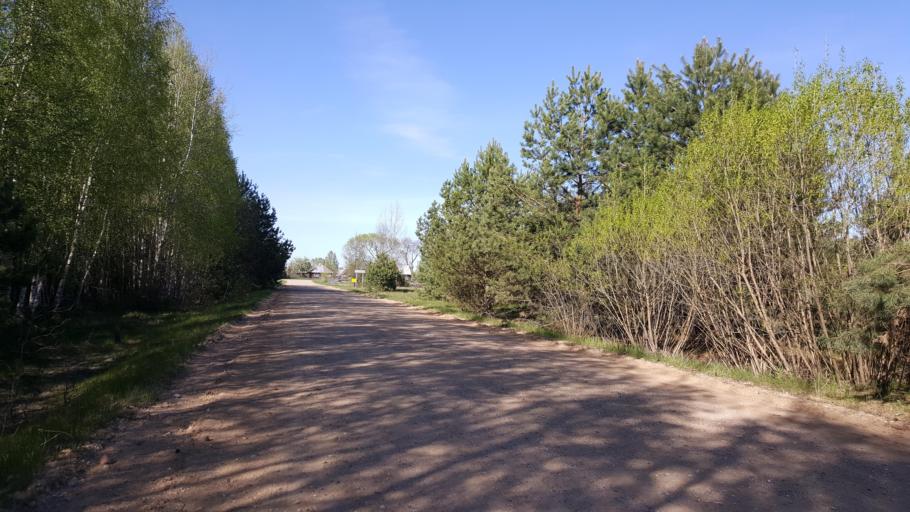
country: BY
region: Brest
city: Kamyanyets
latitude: 52.4392
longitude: 23.8881
